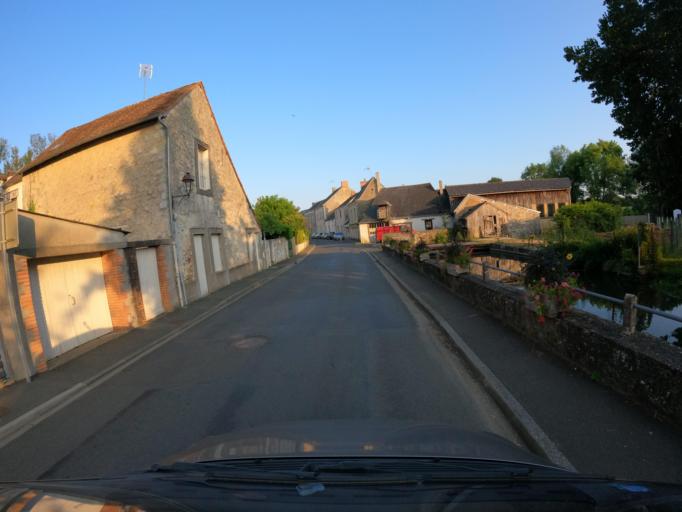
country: FR
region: Pays de la Loire
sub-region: Departement de la Sarthe
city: Parce-sur-Sarthe
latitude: 47.8666
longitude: -0.2080
